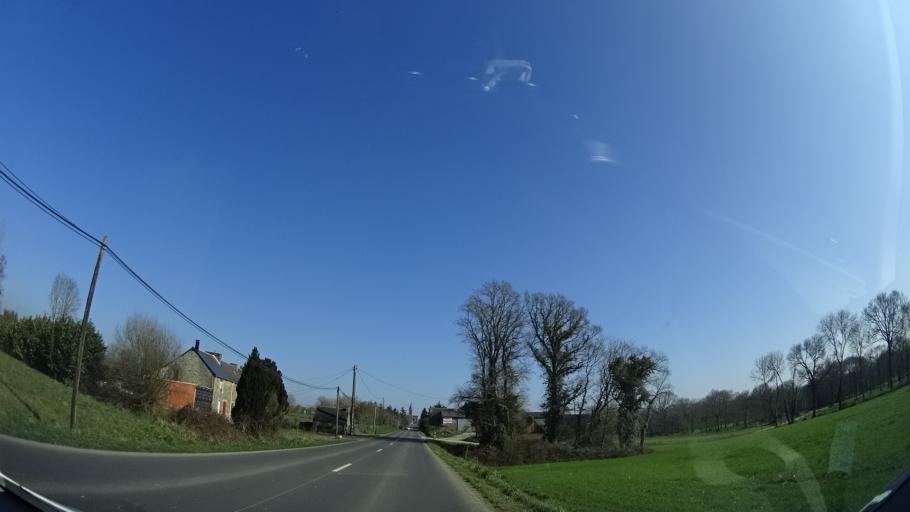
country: FR
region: Brittany
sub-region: Departement d'Ille-et-Vilaine
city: Meillac
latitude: 48.4128
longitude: -1.8240
